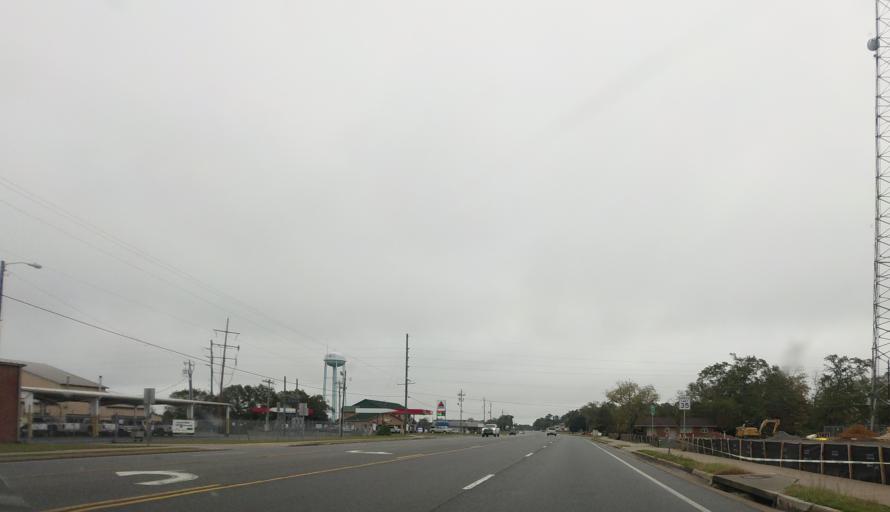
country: US
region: Georgia
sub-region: Taylor County
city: Reynolds
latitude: 32.5584
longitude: -84.0943
